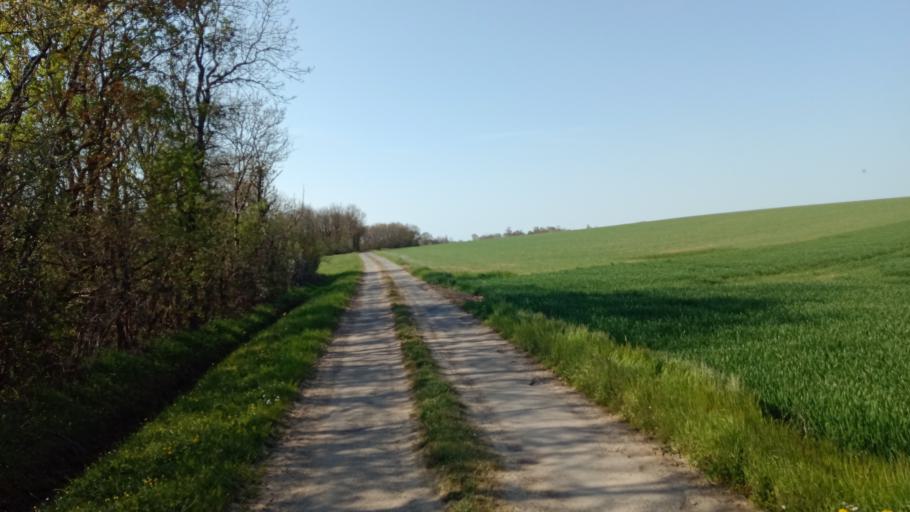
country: FR
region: Poitou-Charentes
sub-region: Departement de la Charente-Maritime
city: Verines
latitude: 46.1612
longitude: -0.9377
